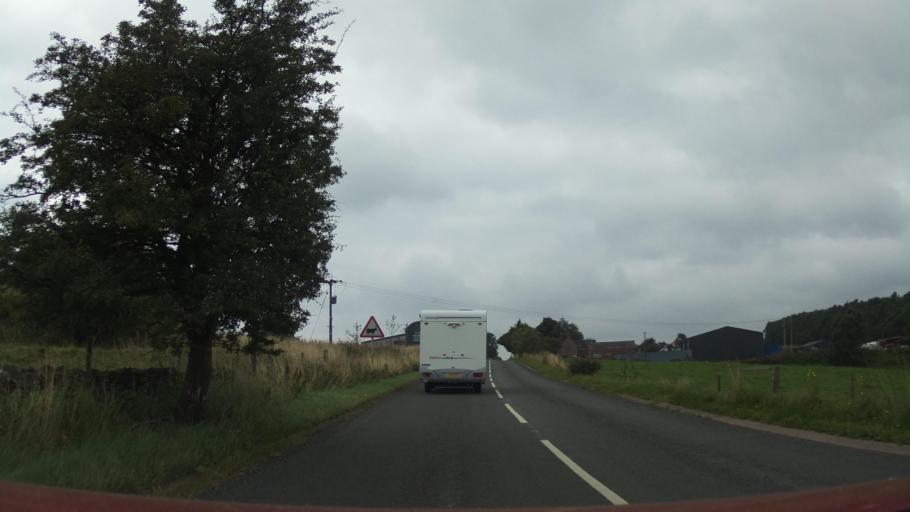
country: GB
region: England
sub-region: Staffordshire
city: Mayfield
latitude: 53.0277
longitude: -1.8665
